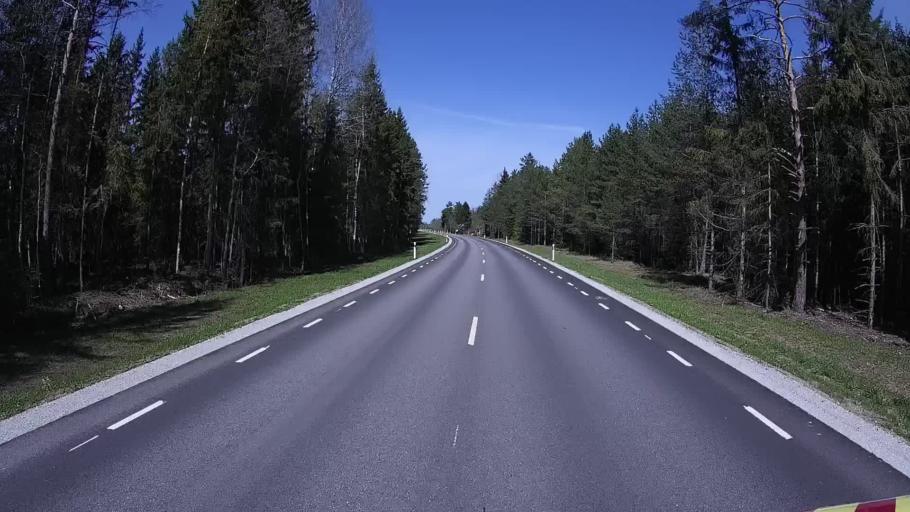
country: EE
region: Harju
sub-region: Nissi vald
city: Turba
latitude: 59.1491
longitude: 24.0776
